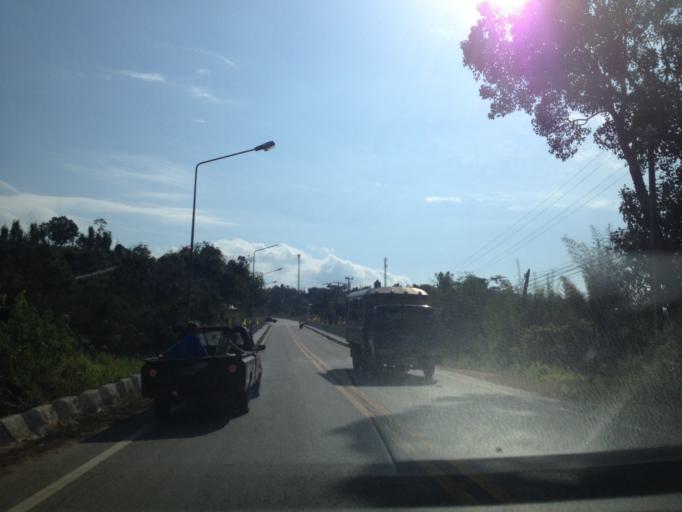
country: TH
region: Mae Hong Son
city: Ban Huai I Huak
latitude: 18.1501
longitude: 98.2478
